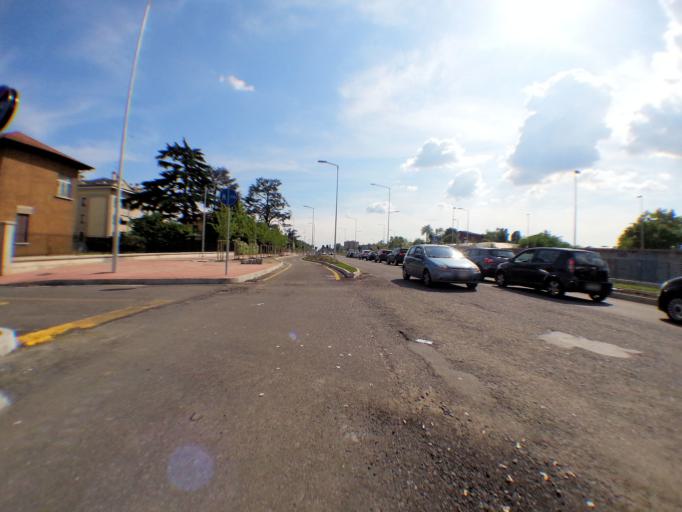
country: IT
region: Lombardy
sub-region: Provincia di Monza e Brianza
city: Monza
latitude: 45.5807
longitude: 9.2498
